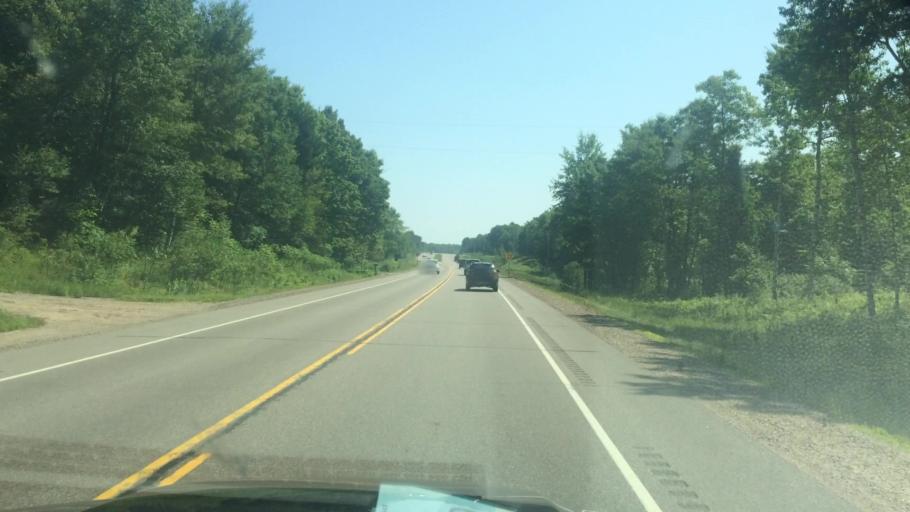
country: US
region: Wisconsin
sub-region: Oneida County
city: Rhinelander
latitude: 45.6169
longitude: -89.4952
